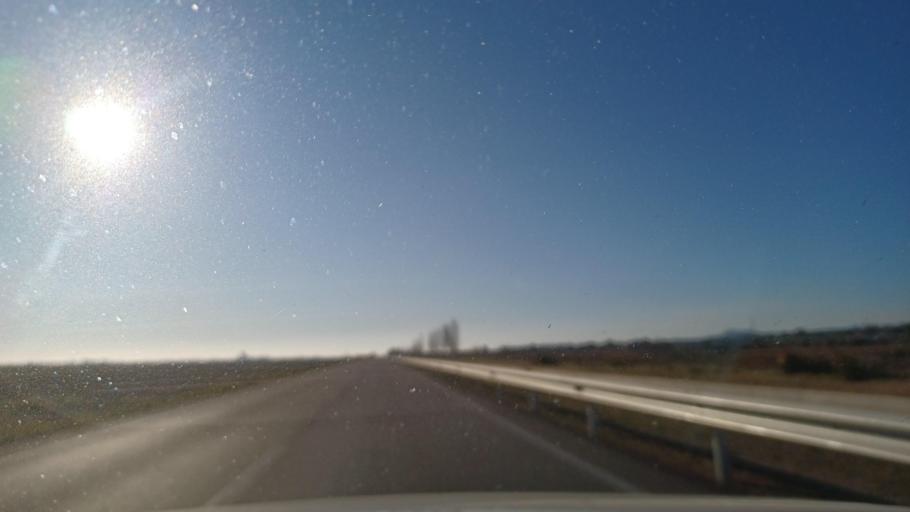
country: ES
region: Catalonia
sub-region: Provincia de Tarragona
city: Sant Carles de la Rapita
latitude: 40.6593
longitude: 0.5926
